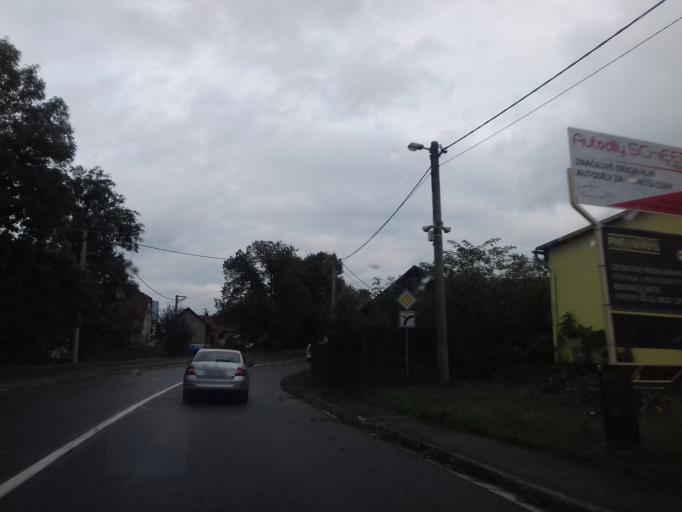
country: CZ
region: Pardubicky
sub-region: Okres Chrudim
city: Chrast
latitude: 49.8949
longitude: 15.9557
